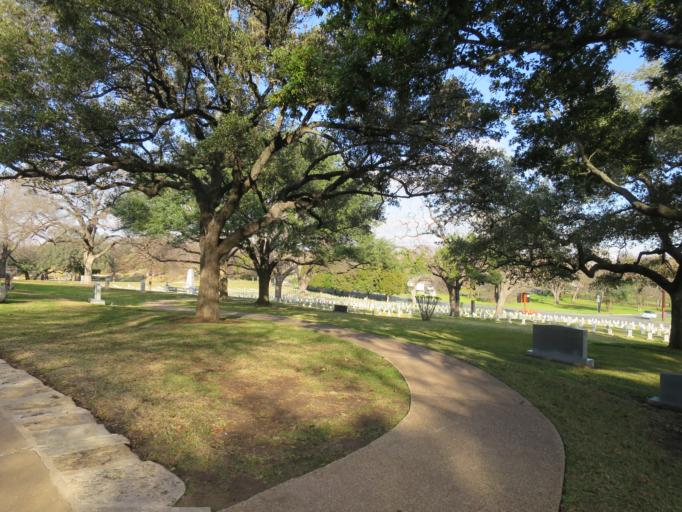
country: US
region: Texas
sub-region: Travis County
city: Austin
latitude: 30.2647
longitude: -97.7267
